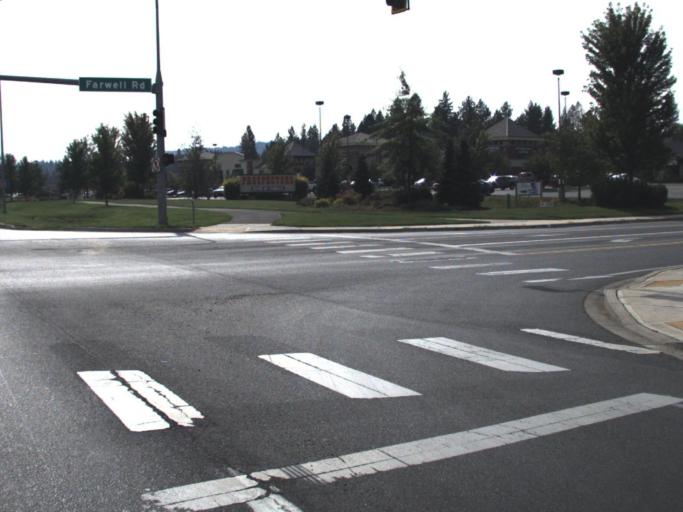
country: US
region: Washington
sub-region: Spokane County
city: Fairwood
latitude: 47.7730
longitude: -117.4031
